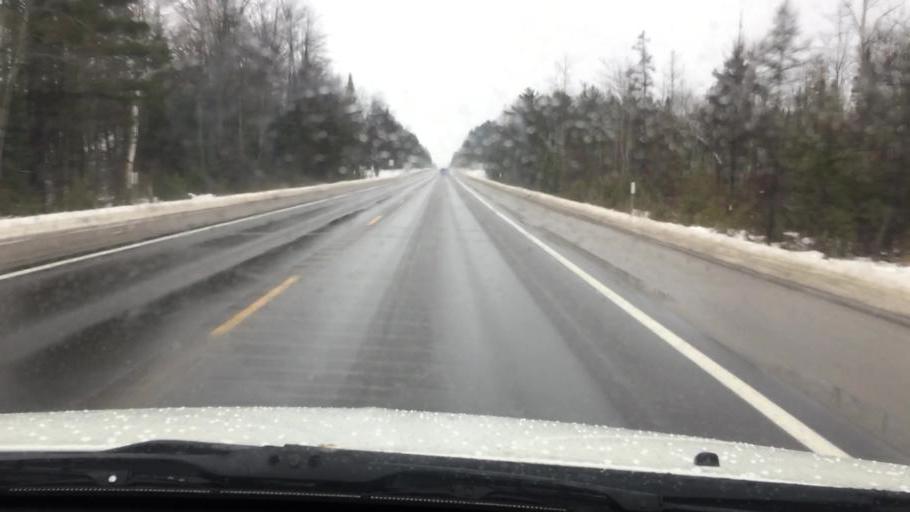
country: US
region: Michigan
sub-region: Kalkaska County
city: Kalkaska
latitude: 44.6982
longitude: -85.2065
